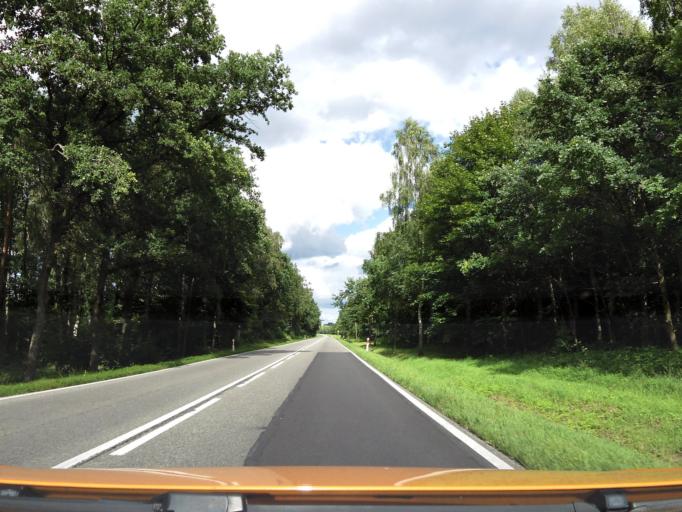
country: PL
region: West Pomeranian Voivodeship
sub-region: Powiat gryficki
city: Brojce
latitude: 53.8917
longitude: 15.4148
